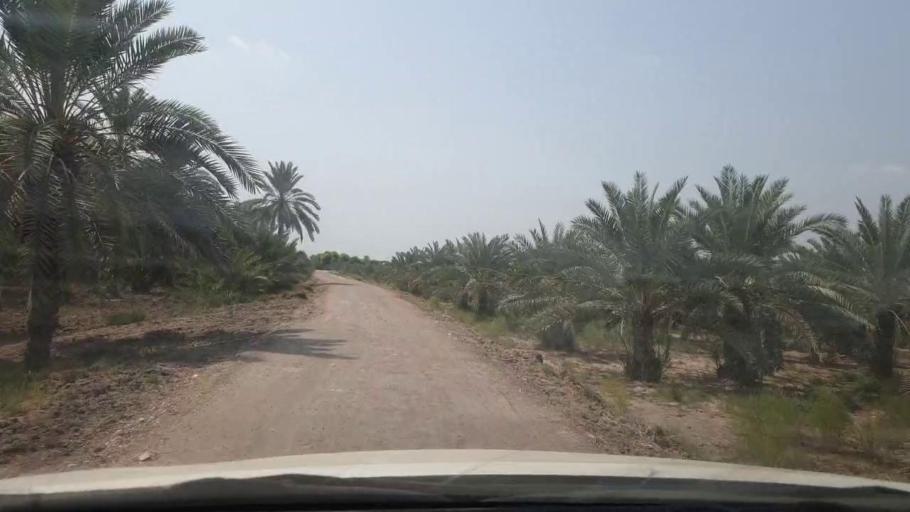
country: PK
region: Sindh
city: Khairpur
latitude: 27.5595
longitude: 68.8505
